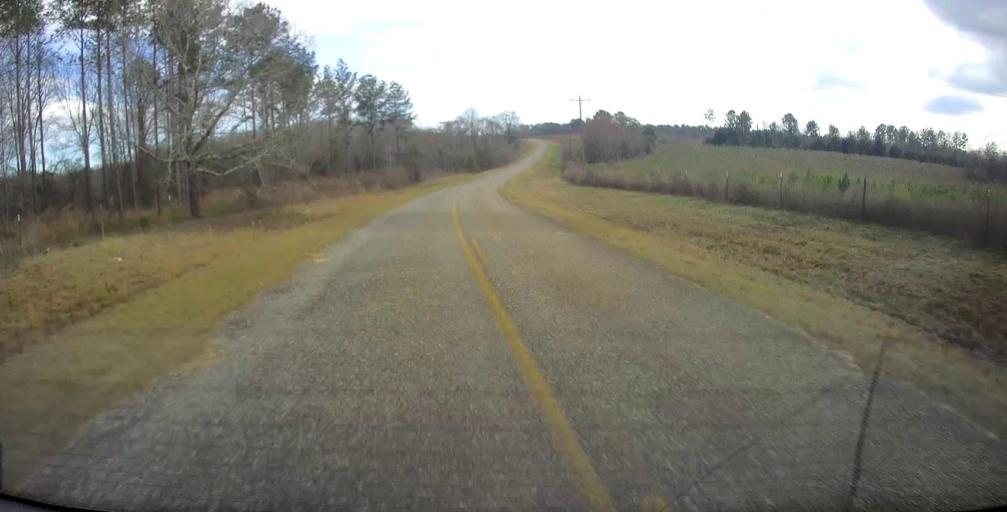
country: US
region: Georgia
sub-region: Marion County
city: Buena Vista
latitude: 32.4171
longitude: -84.4124
